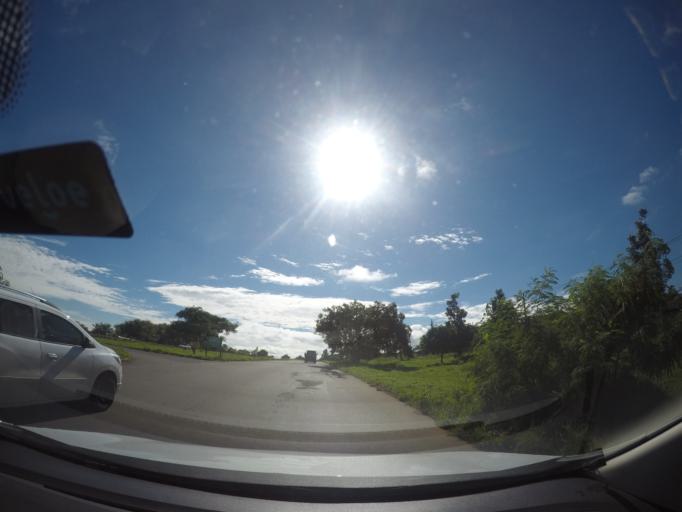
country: BR
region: Goias
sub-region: Senador Canedo
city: Senador Canedo
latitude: -16.6504
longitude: -49.1617
